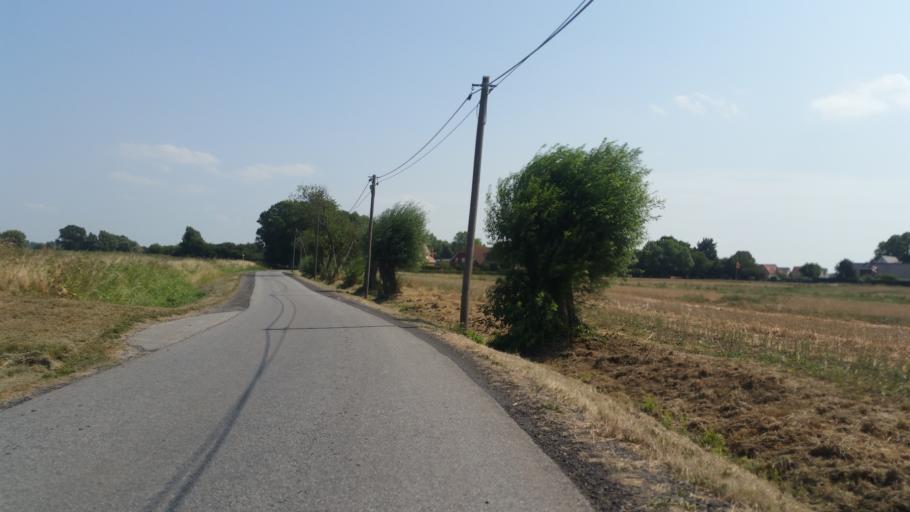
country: DE
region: Mecklenburg-Vorpommern
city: Biendorf
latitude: 54.0947
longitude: 11.6395
